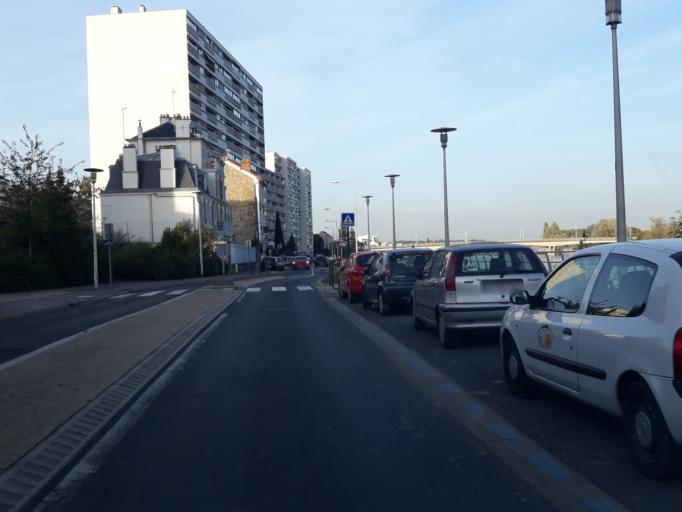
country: FR
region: Ile-de-France
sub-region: Departement de l'Essonne
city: Juvisy-sur-Orge
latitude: 48.6853
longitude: 2.3852
